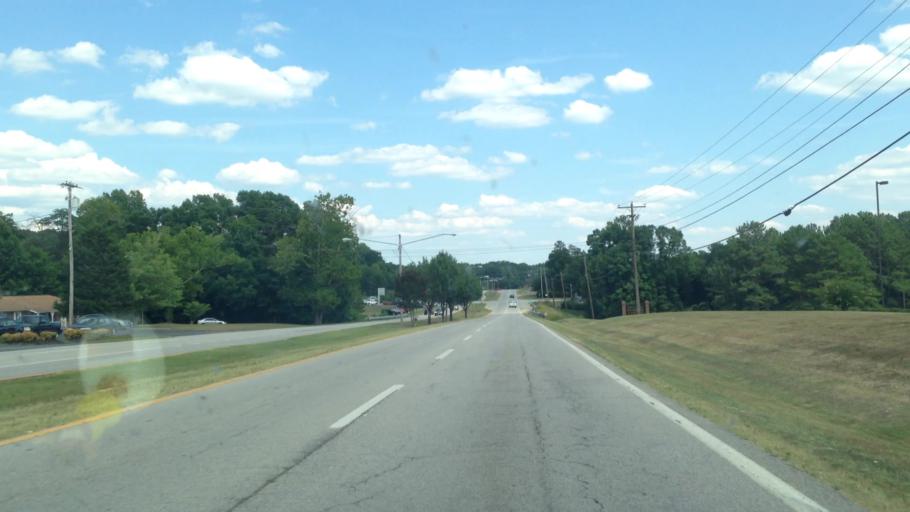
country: US
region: Virginia
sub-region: City of Danville
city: Danville
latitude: 36.5924
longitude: -79.4629
